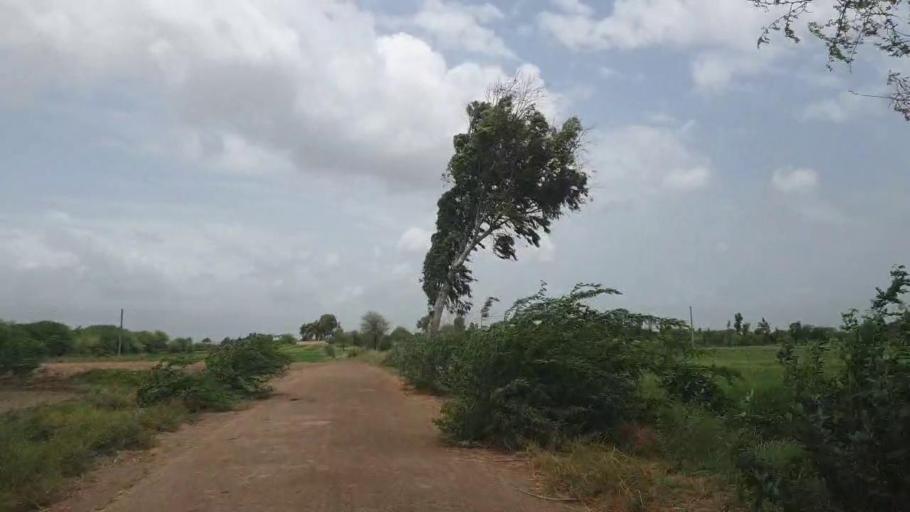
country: PK
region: Sindh
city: Badin
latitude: 24.6662
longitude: 68.8919
